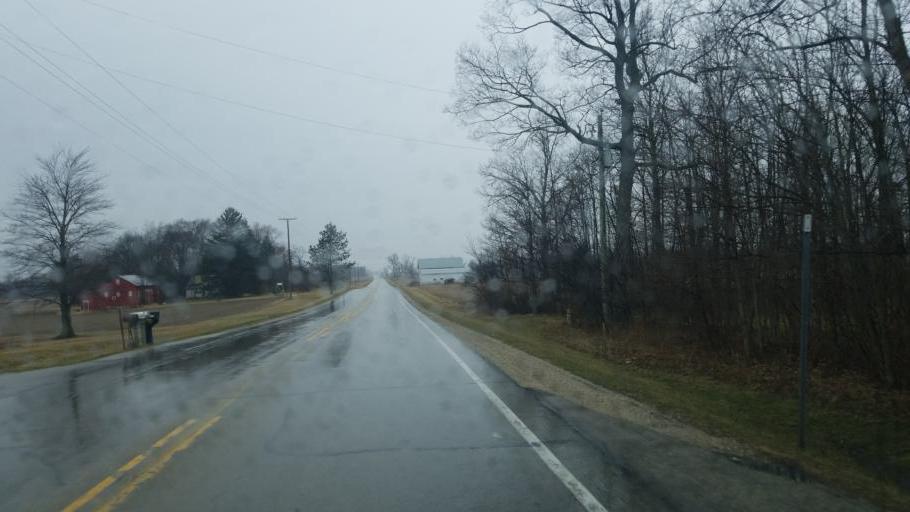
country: US
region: Indiana
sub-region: Adams County
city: Berne
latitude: 40.6562
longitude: -85.0249
